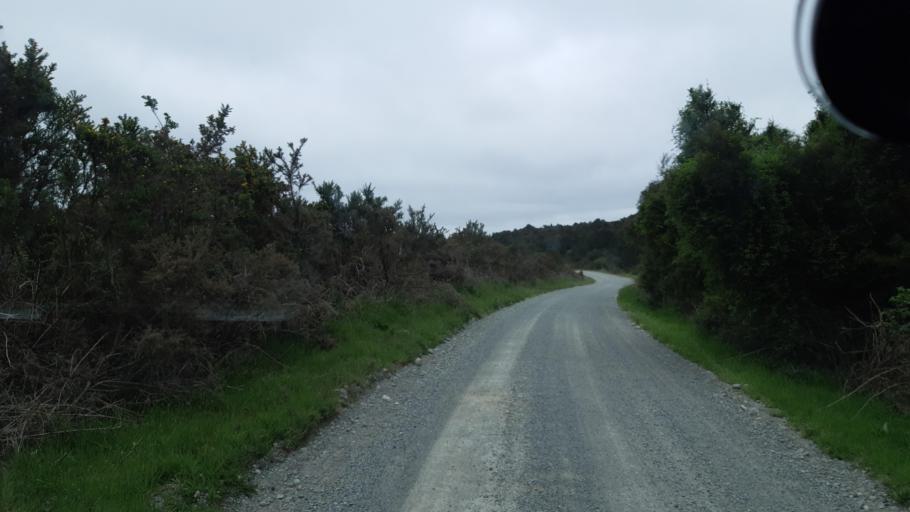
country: NZ
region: West Coast
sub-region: Grey District
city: Greymouth
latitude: -42.6347
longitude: 171.2849
